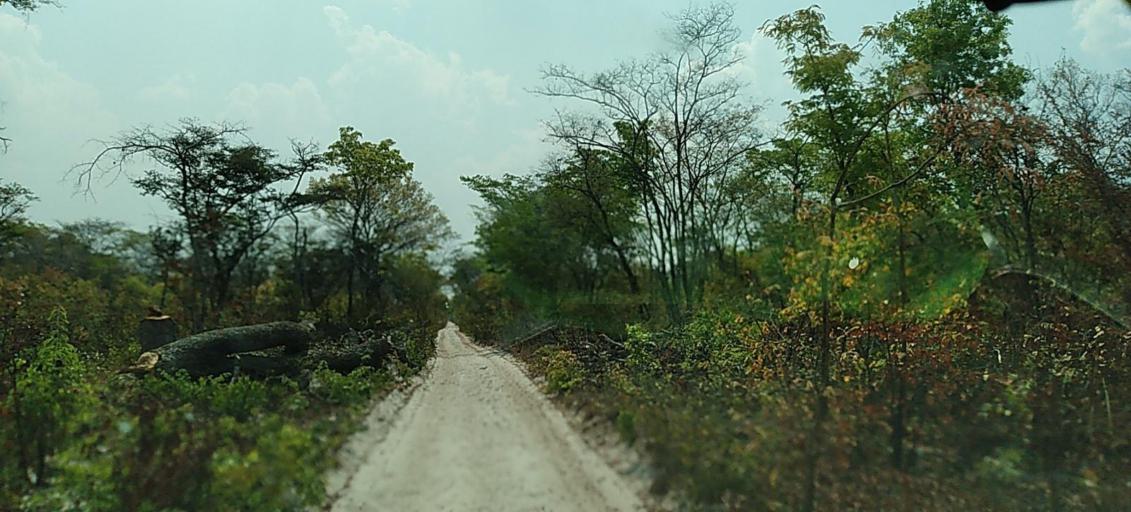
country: ZM
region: North-Western
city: Kabompo
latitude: -13.3914
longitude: 23.7856
